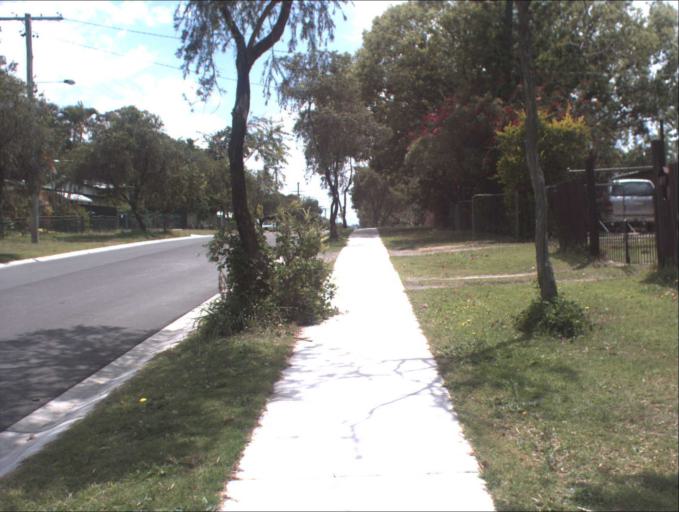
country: AU
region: Queensland
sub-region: Logan
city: Woodridge
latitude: -27.6315
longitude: 153.0965
